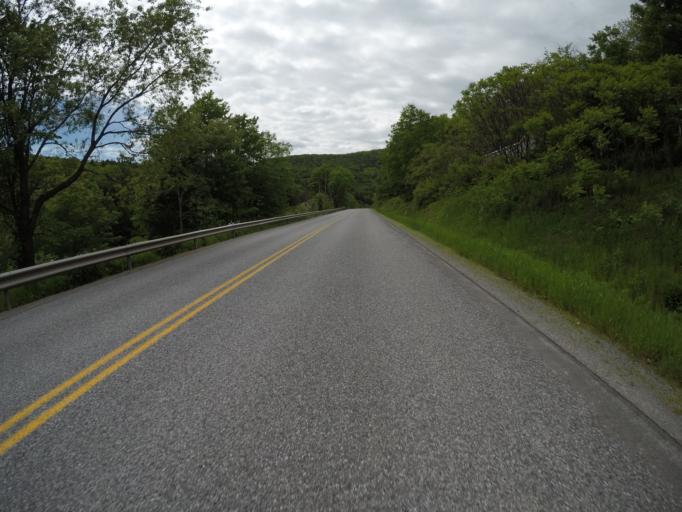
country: US
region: New York
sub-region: Delaware County
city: Stamford
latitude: 42.1847
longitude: -74.5861
